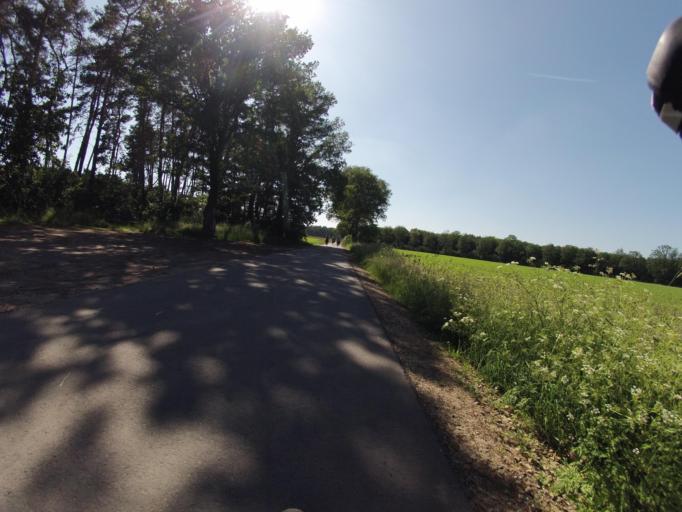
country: DE
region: North Rhine-Westphalia
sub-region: Regierungsbezirk Munster
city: Dreierwalde
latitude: 52.2602
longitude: 7.5263
